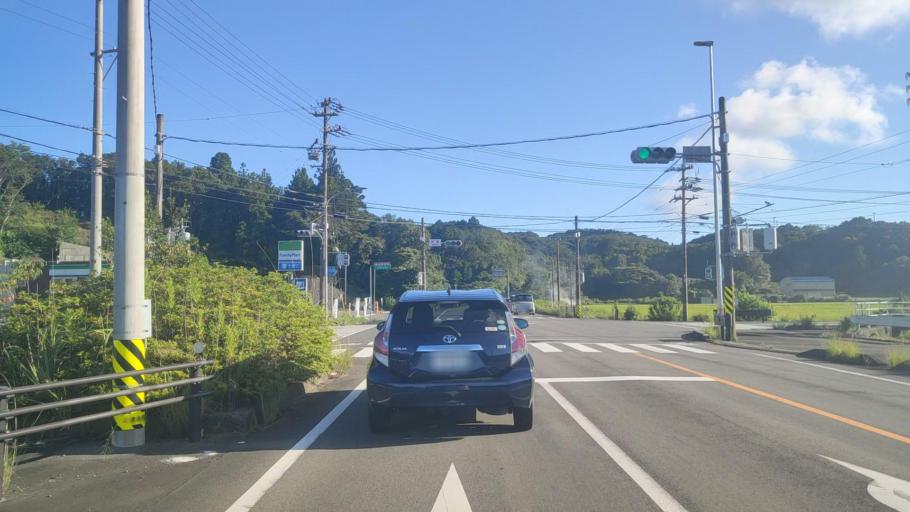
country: JP
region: Mie
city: Toba
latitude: 34.3523
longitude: 136.8447
